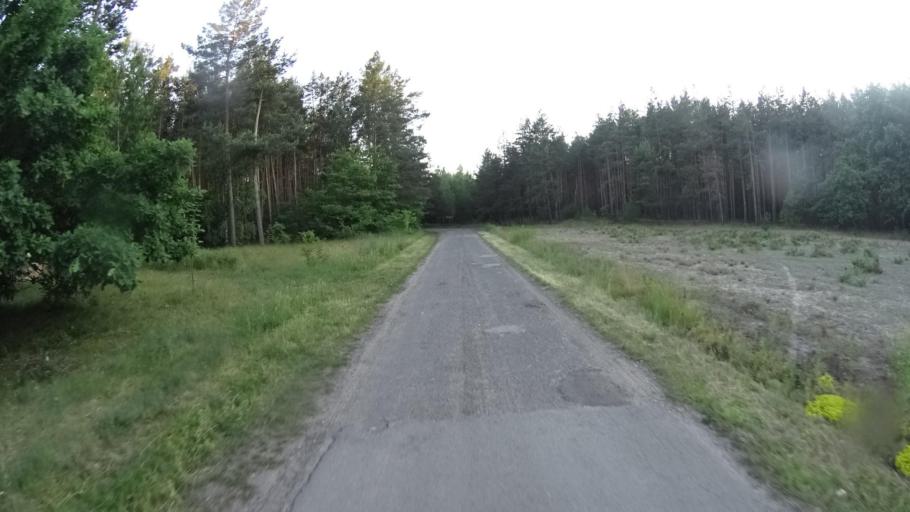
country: PL
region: Masovian Voivodeship
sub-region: Powiat warszawski zachodni
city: Jozefow
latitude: 52.2729
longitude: 20.6967
